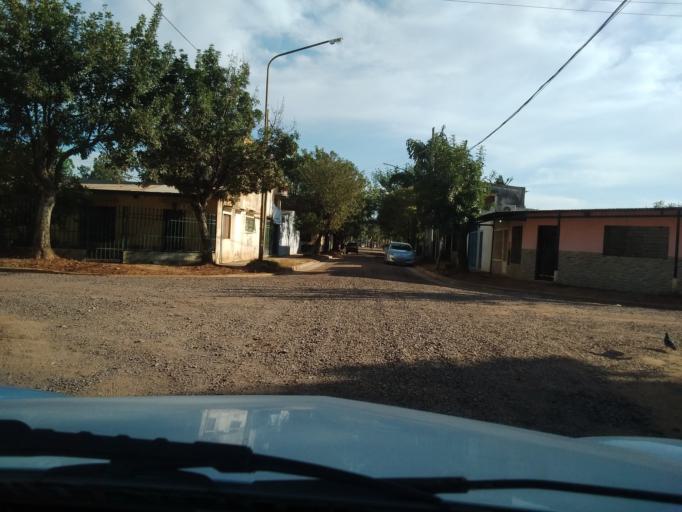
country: AR
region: Corrientes
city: Corrientes
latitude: -27.4871
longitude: -58.7834
